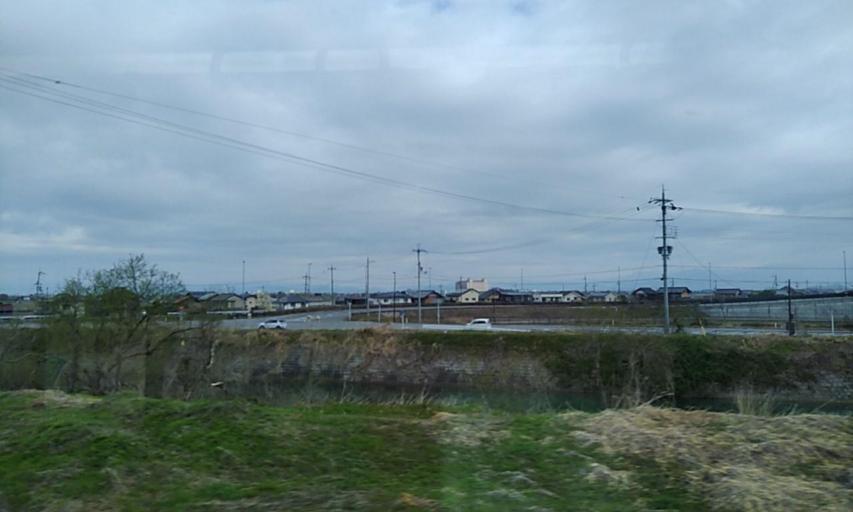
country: JP
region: Shiga Prefecture
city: Hikone
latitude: 35.2982
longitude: 136.2720
